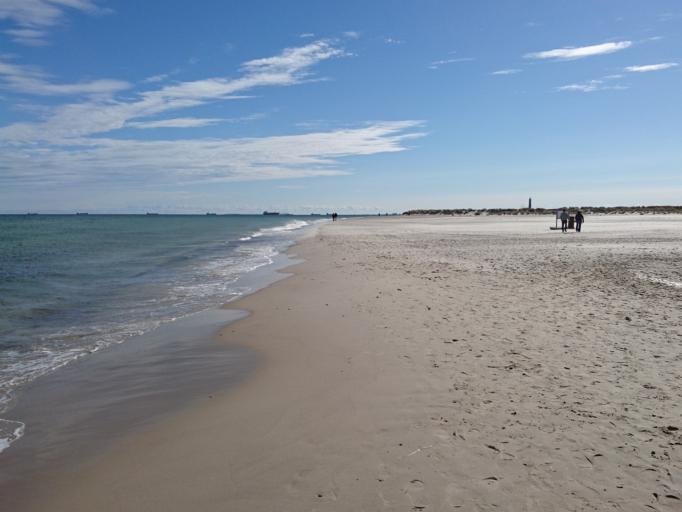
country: DK
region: North Denmark
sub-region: Frederikshavn Kommune
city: Skagen
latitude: 57.7469
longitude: 10.6521
